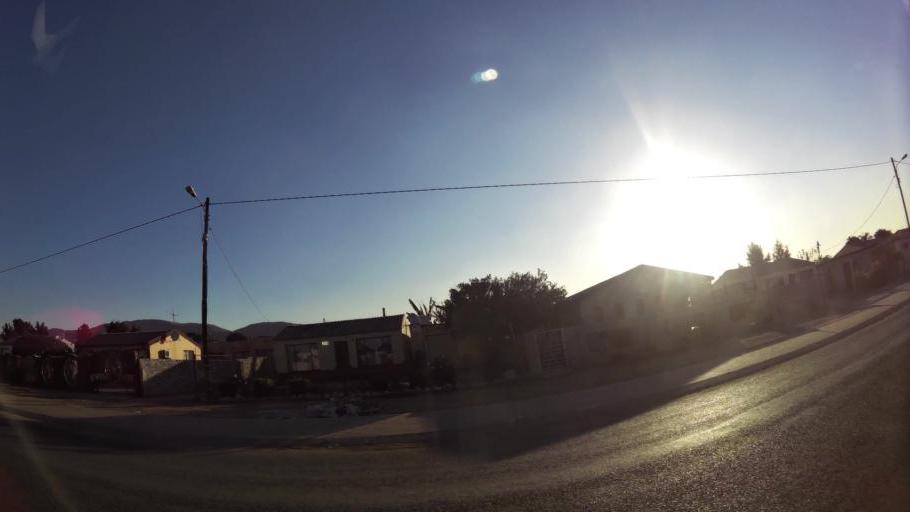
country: ZA
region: North-West
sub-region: Bojanala Platinum District Municipality
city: Rustenburg
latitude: -25.6312
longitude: 27.2154
